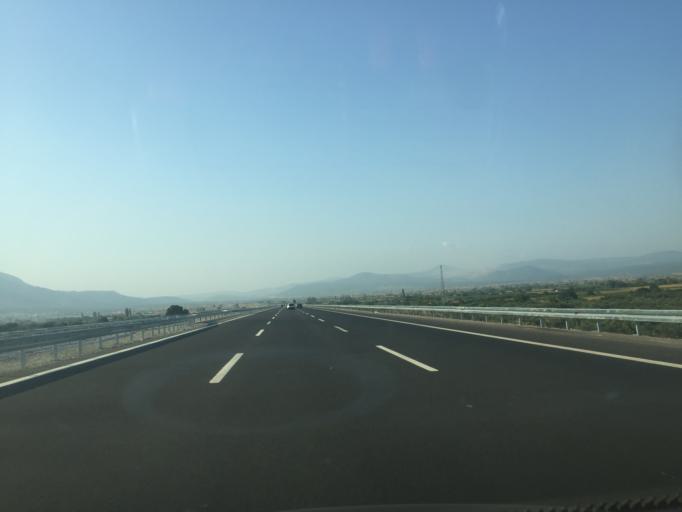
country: TR
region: Manisa
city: Kirkagac
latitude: 39.0733
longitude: 27.7167
